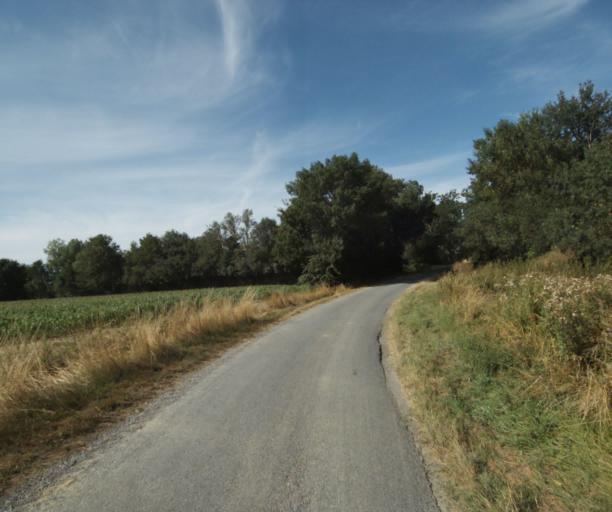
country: FR
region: Midi-Pyrenees
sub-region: Departement du Tarn
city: Puylaurens
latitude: 43.5193
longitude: 2.0374
